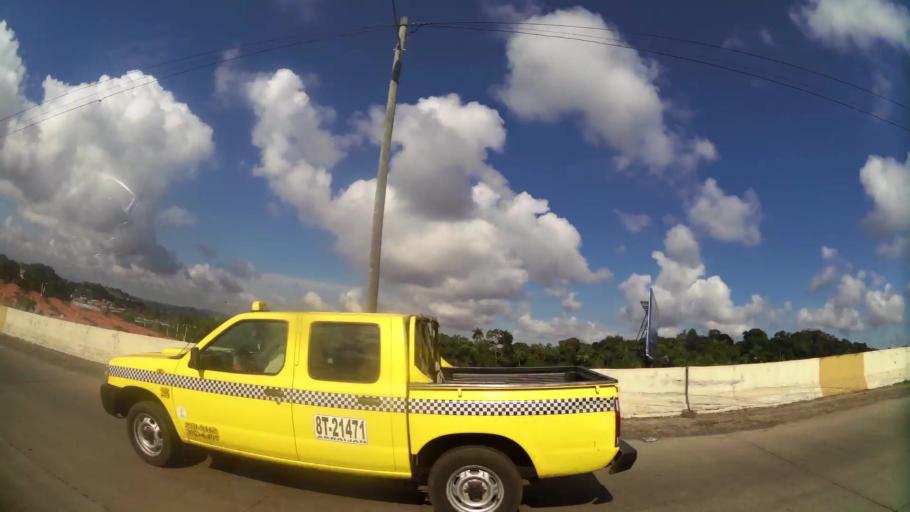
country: PA
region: Panama
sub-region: Distrito Arraijan
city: Arraijan
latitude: 8.9548
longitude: -79.6619
